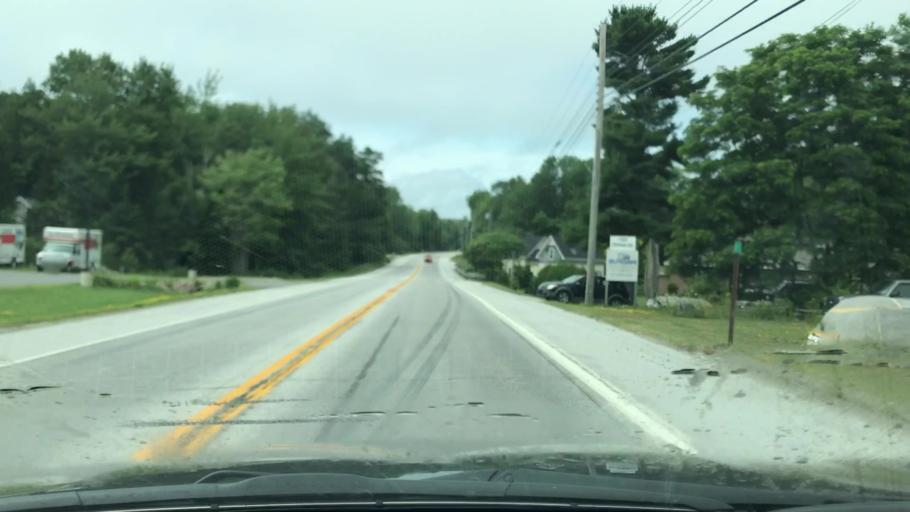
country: US
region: Maine
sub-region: Waldo County
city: Northport
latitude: 44.3366
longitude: -68.9596
